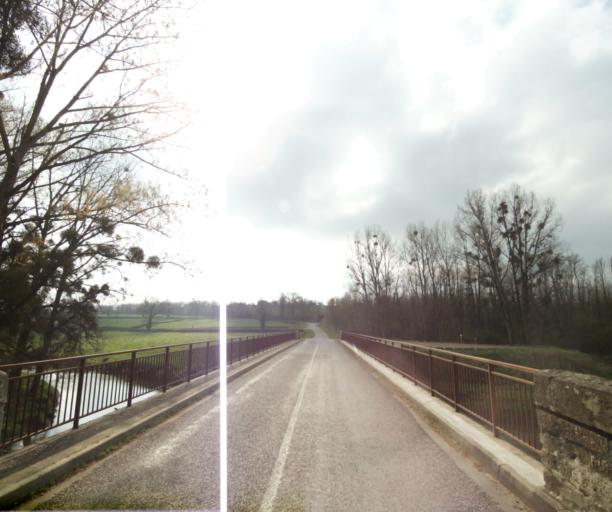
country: FR
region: Bourgogne
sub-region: Departement de Saone-et-Loire
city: Charolles
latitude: 46.4073
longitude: 4.2106
